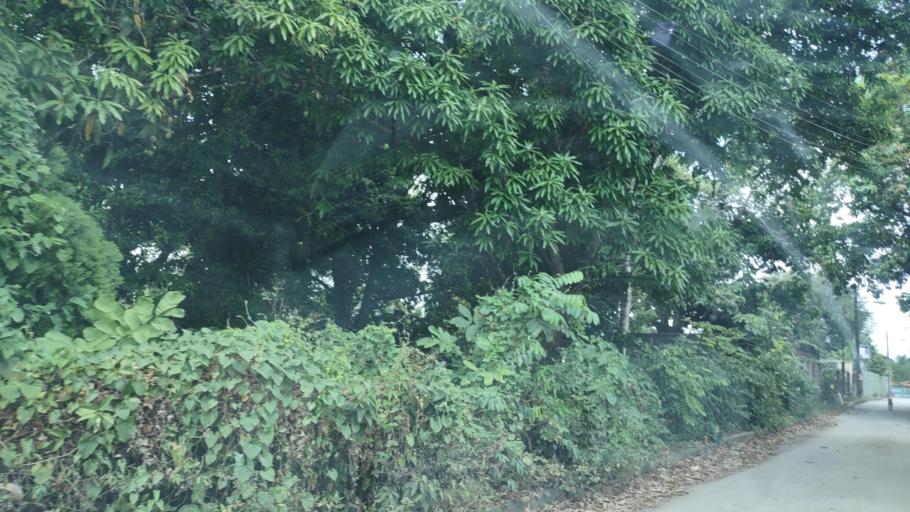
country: MX
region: Veracruz
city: Las Choapas
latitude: 17.9247
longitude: -94.0969
